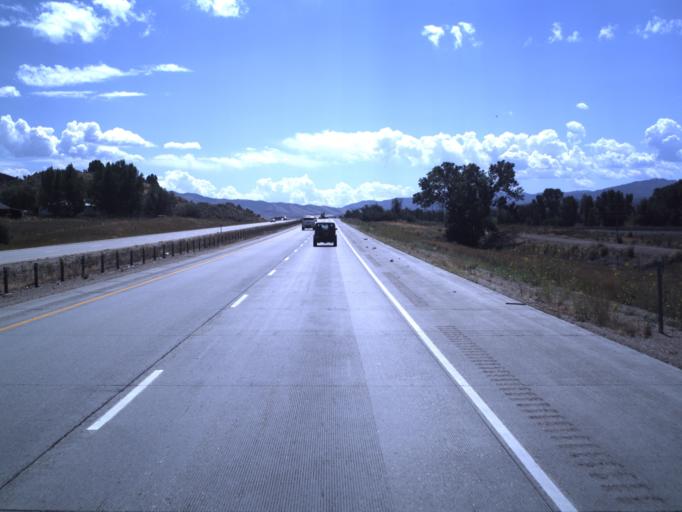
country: US
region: Utah
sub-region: Morgan County
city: Mountain Green
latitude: 41.0911
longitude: -111.7367
